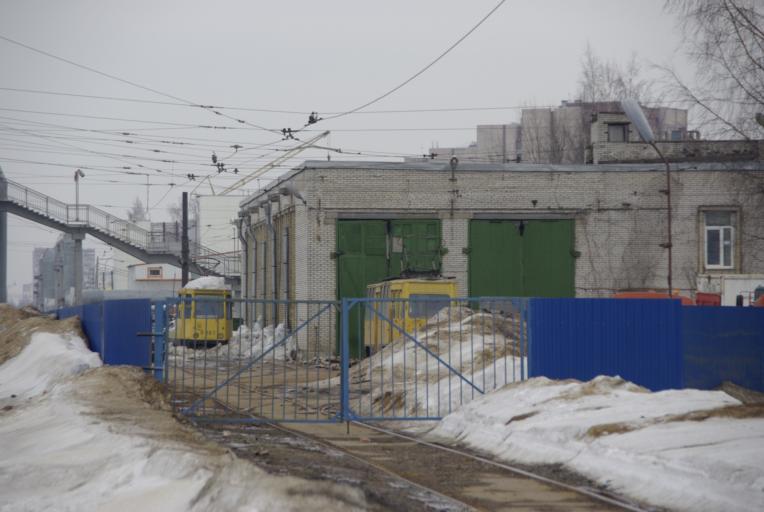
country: RU
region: Leningrad
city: Parnas
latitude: 60.0599
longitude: 30.3438
